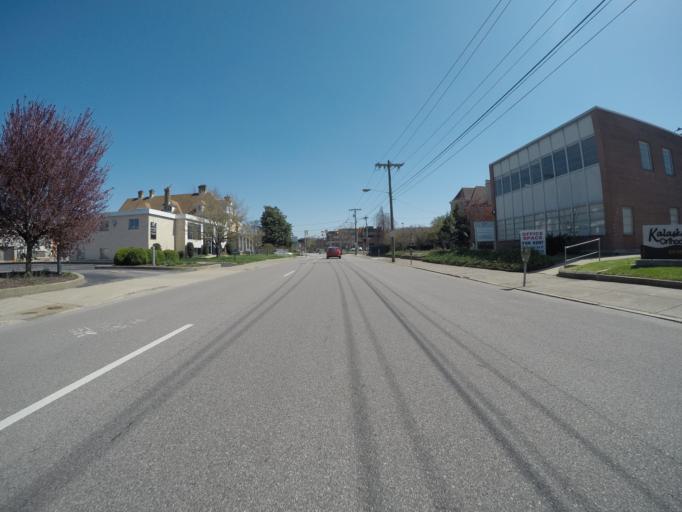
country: US
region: West Virginia
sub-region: Kanawha County
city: Charleston
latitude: 38.3447
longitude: -81.6304
